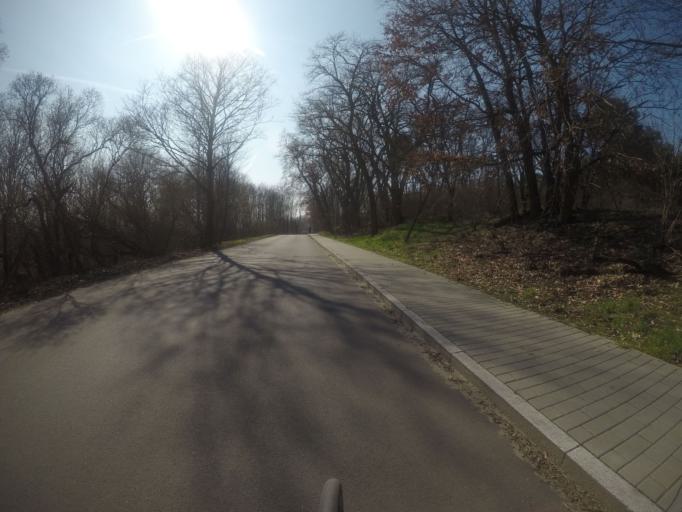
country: DE
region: Berlin
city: Muggelheim
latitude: 52.3888
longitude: 13.7033
